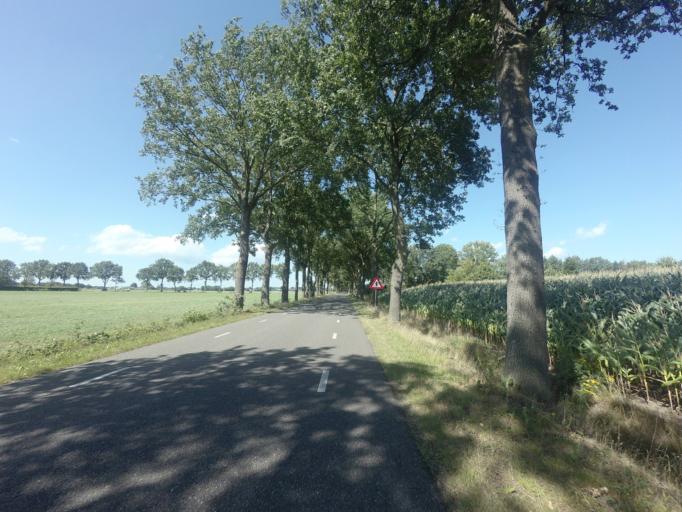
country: NL
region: Overijssel
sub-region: Gemeente Twenterand
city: Den Ham
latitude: 52.5538
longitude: 6.4375
